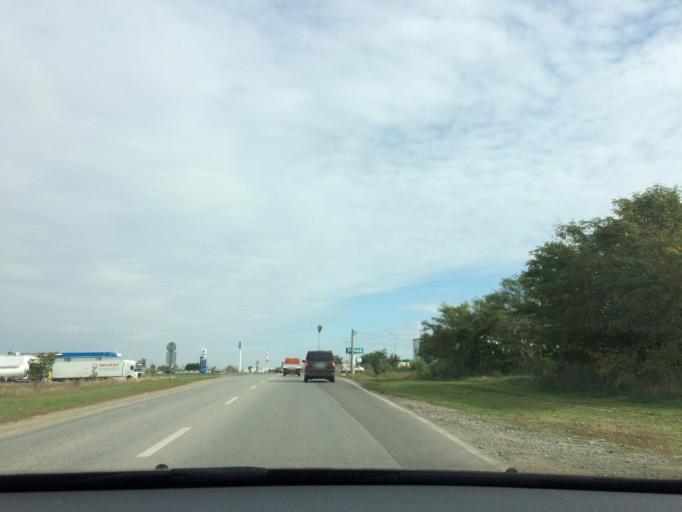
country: RO
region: Timis
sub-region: Comuna Dumbravita
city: Dumbravita
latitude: 45.8118
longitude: 21.2607
